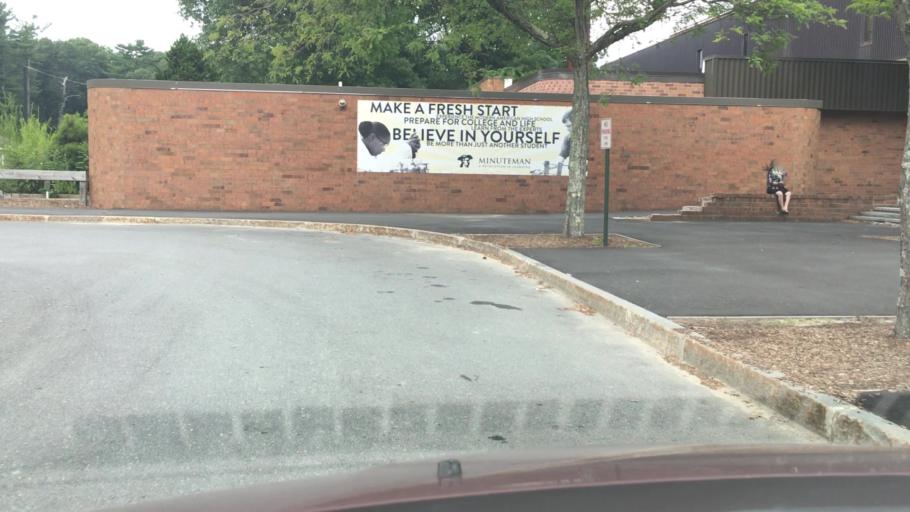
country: US
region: Massachusetts
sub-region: Middlesex County
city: Lincoln
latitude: 42.4454
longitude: -71.2690
